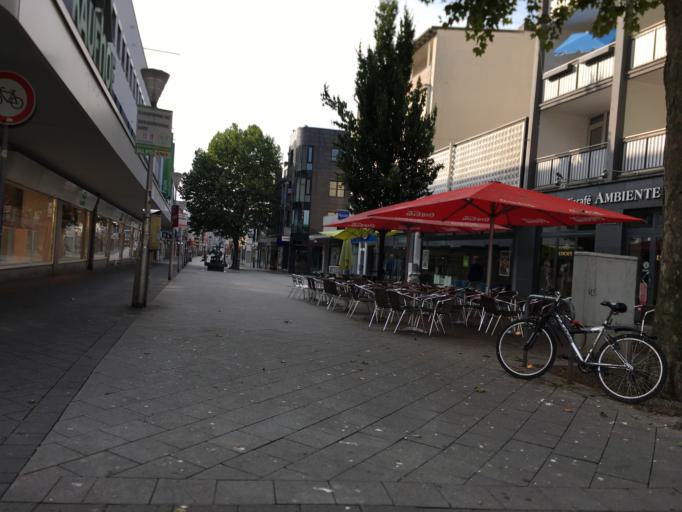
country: DE
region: North Rhine-Westphalia
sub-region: Regierungsbezirk Koln
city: Dueren
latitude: 50.8048
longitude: 6.4834
